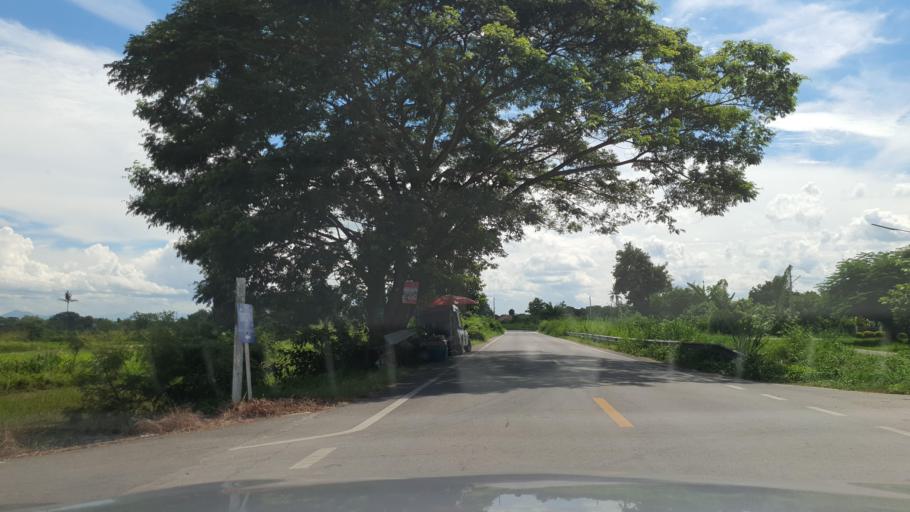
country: TH
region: Chiang Mai
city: San Pa Tong
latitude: 18.5977
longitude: 98.8972
